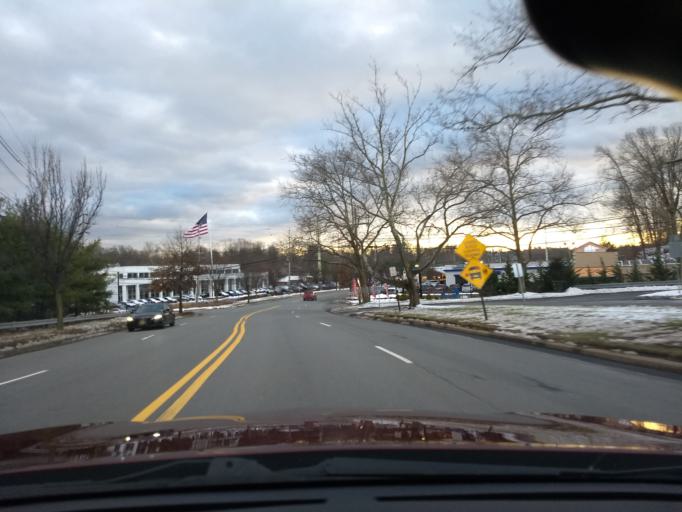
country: US
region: New Jersey
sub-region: Morris County
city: Morristown
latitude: 40.8044
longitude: -74.4645
